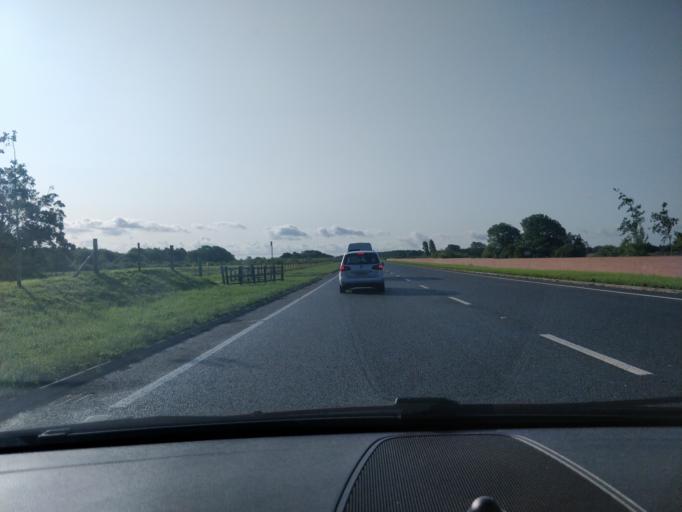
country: GB
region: England
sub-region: Sefton
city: Thornton
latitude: 53.5032
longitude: -2.9921
